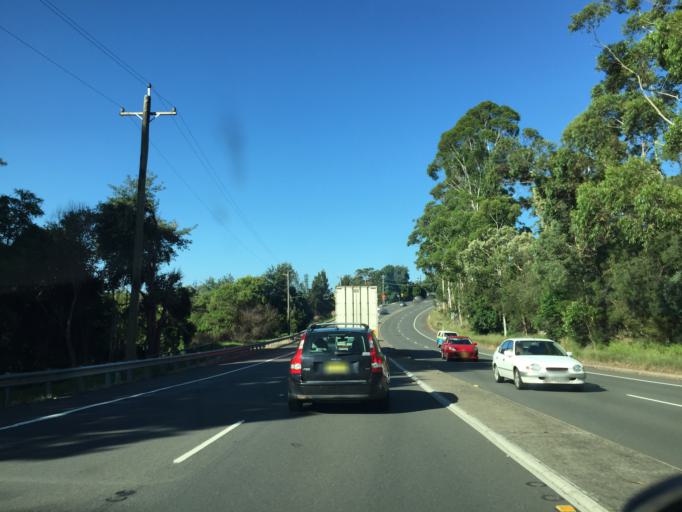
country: AU
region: New South Wales
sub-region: Blue Mountains Municipality
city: Blaxland
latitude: -33.6999
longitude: 150.5609
